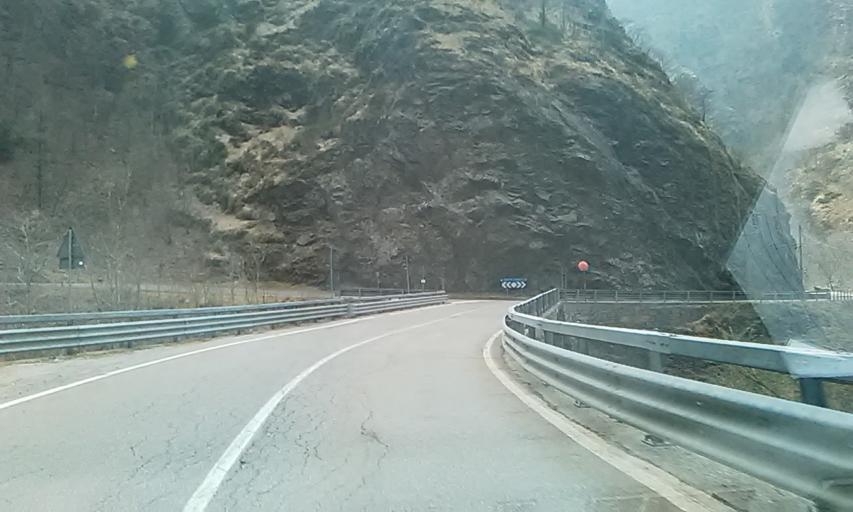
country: IT
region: Piedmont
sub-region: Provincia di Vercelli
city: Cervatto
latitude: 45.8797
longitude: 8.1763
